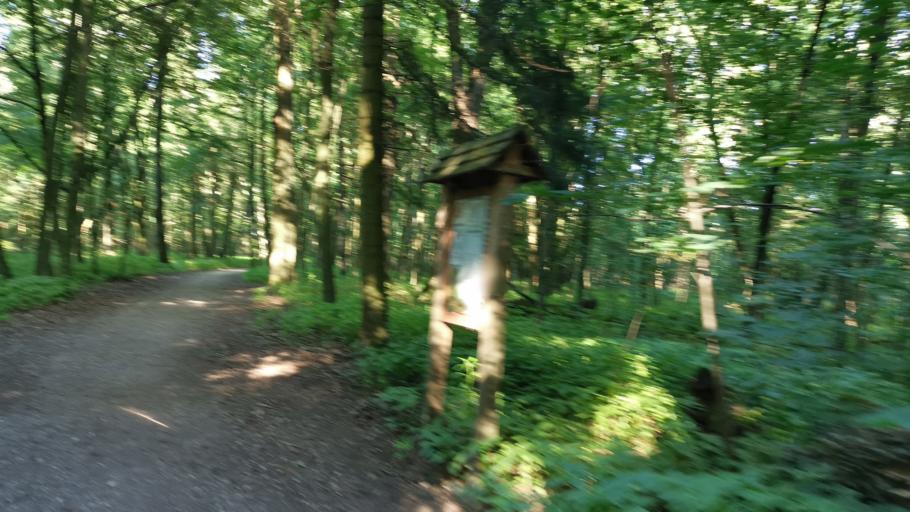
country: DE
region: Bavaria
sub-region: Regierungsbezirk Mittelfranken
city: Stein
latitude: 49.4135
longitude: 11.0265
